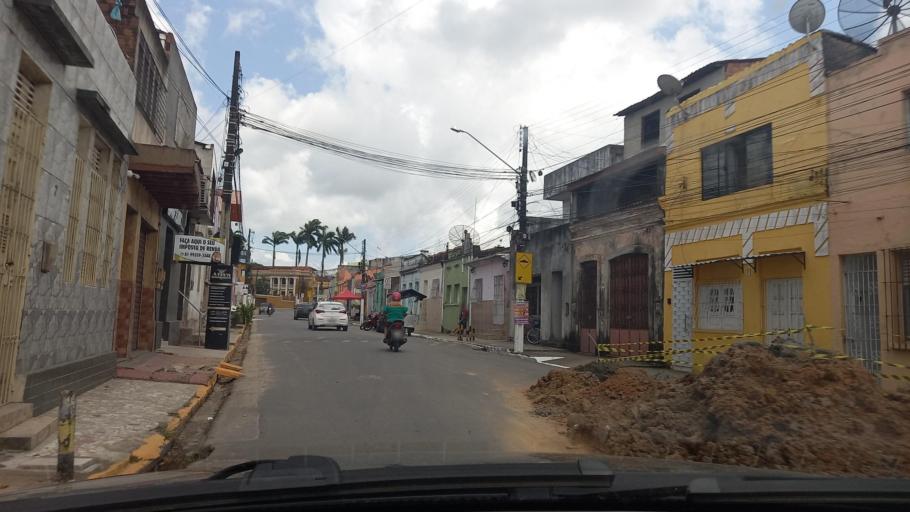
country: BR
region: Pernambuco
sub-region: Goiana
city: Goiana
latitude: -7.5571
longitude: -35.0007
